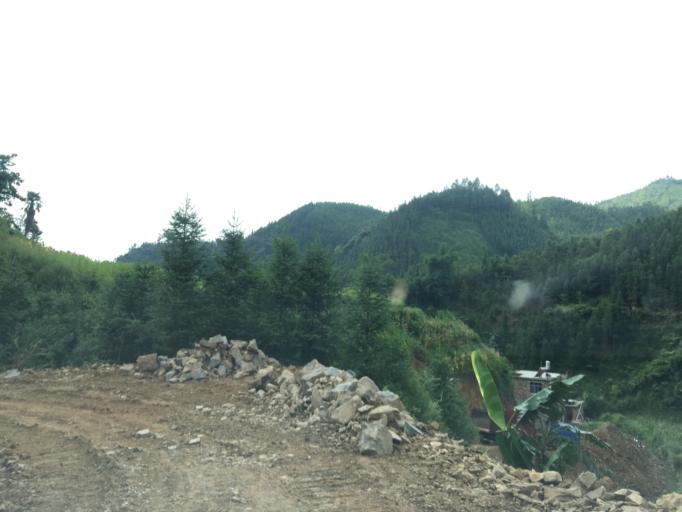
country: CN
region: Guangxi Zhuangzu Zizhiqu
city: Xinzhou
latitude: 24.8687
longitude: 105.8665
